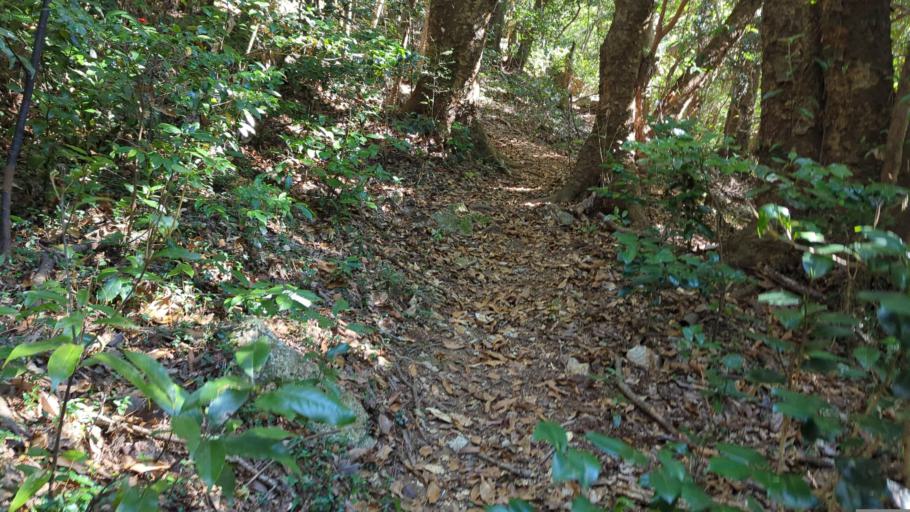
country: JP
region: Aichi
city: Toyohashi
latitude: 34.7705
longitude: 137.4498
